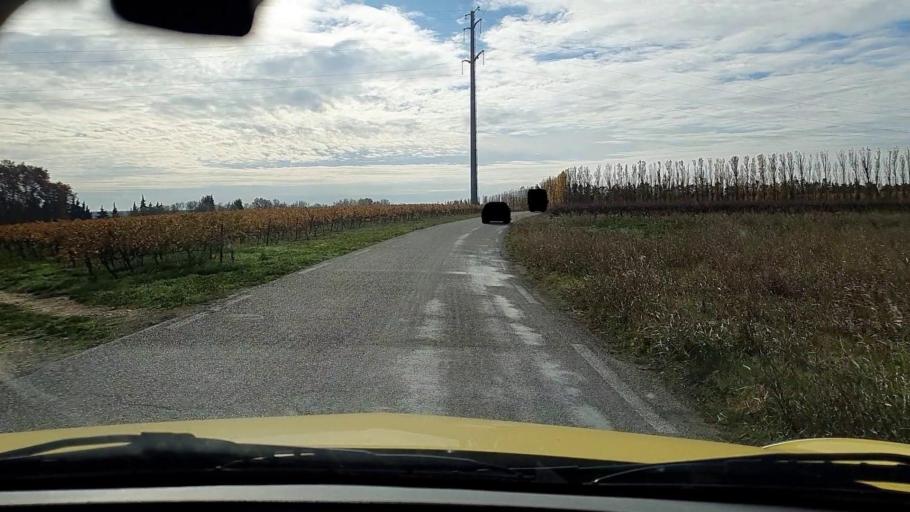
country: FR
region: Languedoc-Roussillon
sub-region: Departement du Gard
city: Jonquieres-Saint-Vincent
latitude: 43.8436
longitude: 4.5713
